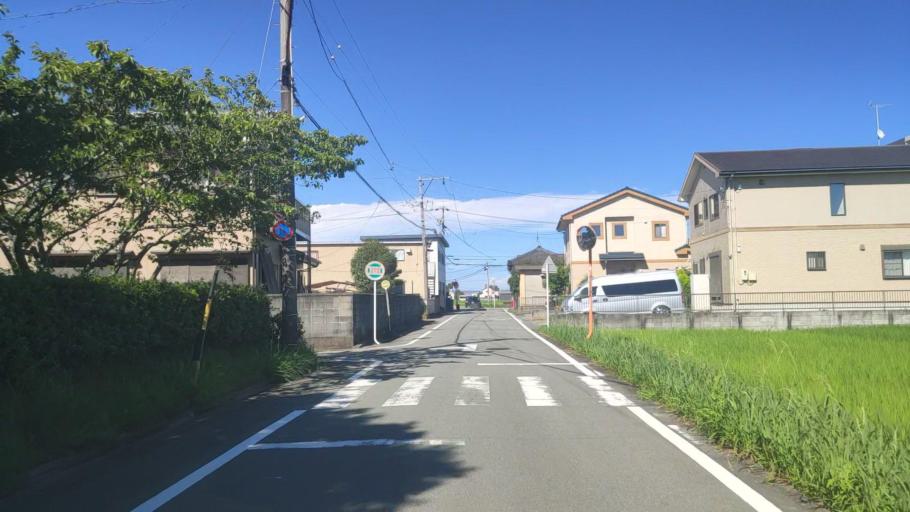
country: JP
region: Mie
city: Ise
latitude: 34.5114
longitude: 136.7155
